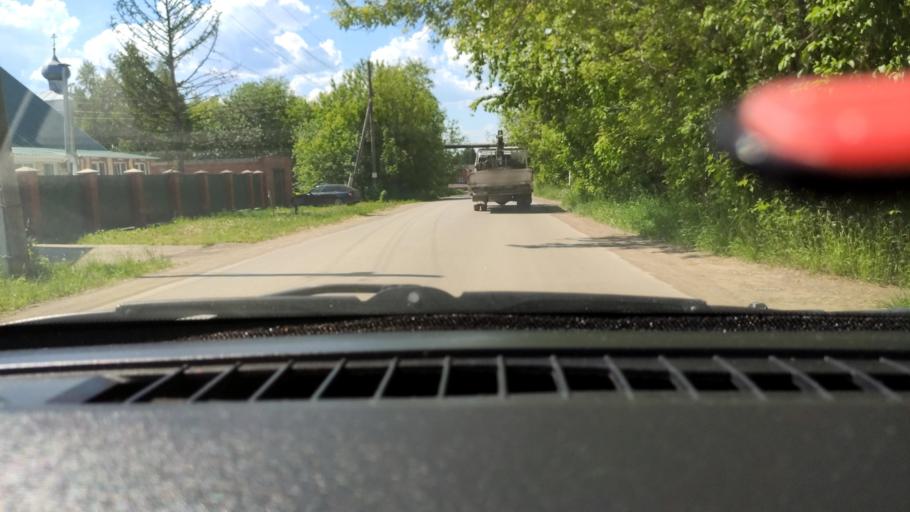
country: RU
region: Perm
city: Sylva
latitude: 58.0334
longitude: 56.7619
